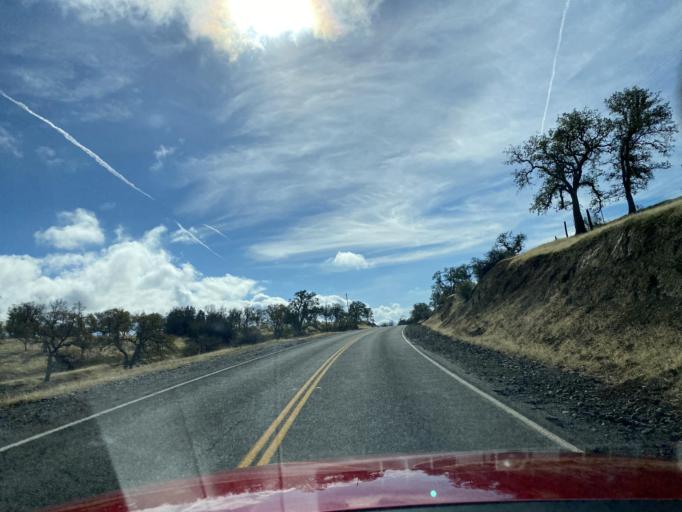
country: US
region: California
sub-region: Glenn County
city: Willows
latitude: 39.4811
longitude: -122.5152
